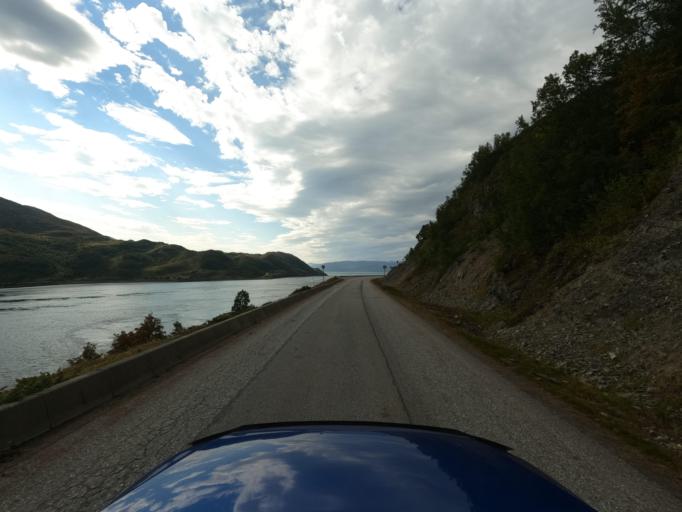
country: NO
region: Finnmark Fylke
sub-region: Kvalsund
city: Kvalsund
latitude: 70.5094
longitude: 23.9142
